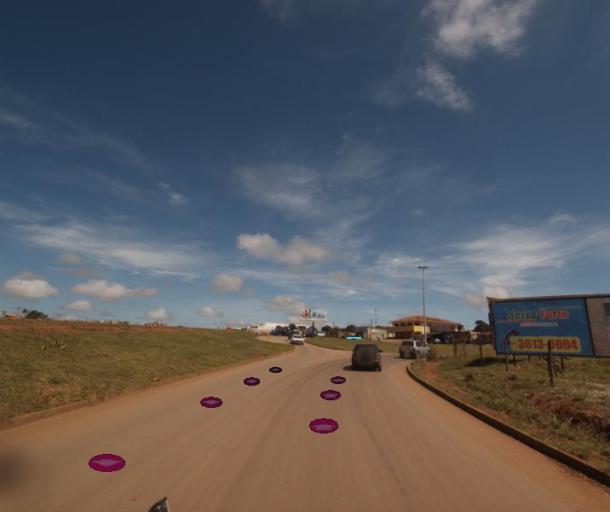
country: BR
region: Federal District
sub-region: Brasilia
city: Brasilia
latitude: -15.7352
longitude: -48.2778
